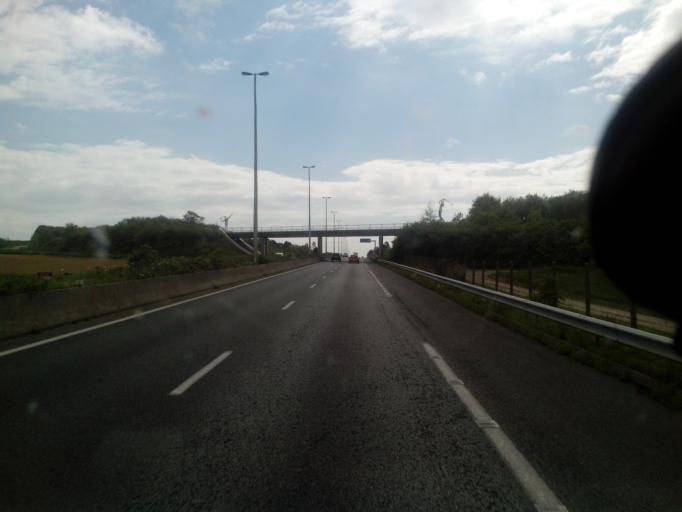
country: FR
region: Nord-Pas-de-Calais
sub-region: Departement du Pas-de-Calais
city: Ferques
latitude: 50.8653
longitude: 1.7415
